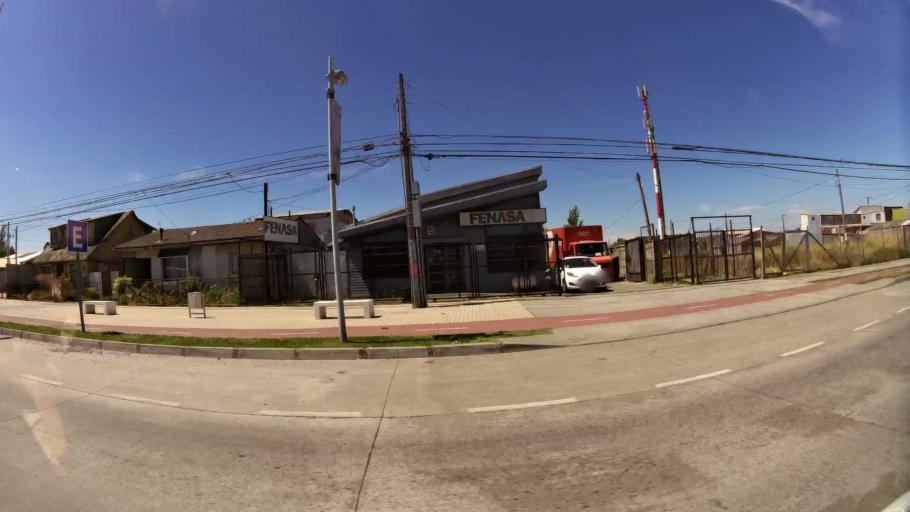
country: CL
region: Biobio
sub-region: Provincia de Concepcion
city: Talcahuano
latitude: -36.7431
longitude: -73.0976
